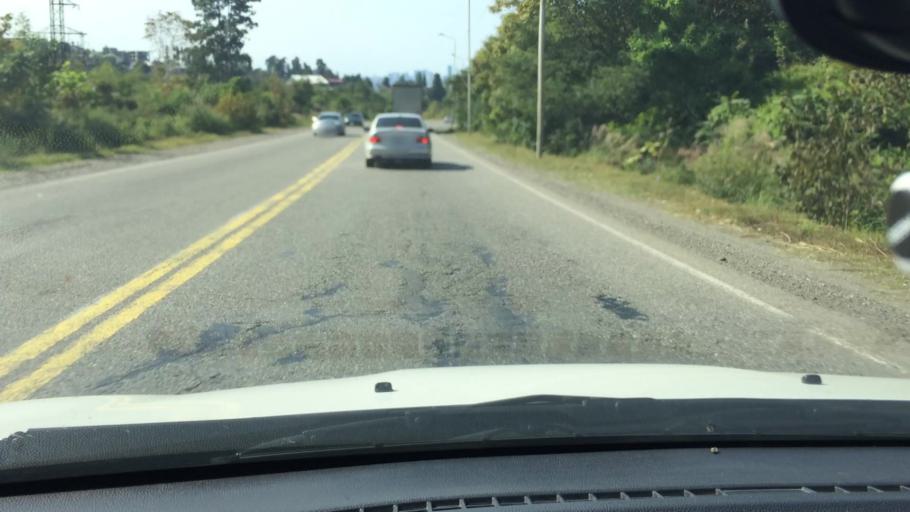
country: GE
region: Ajaria
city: Makhinjauri
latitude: 41.6881
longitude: 41.7110
